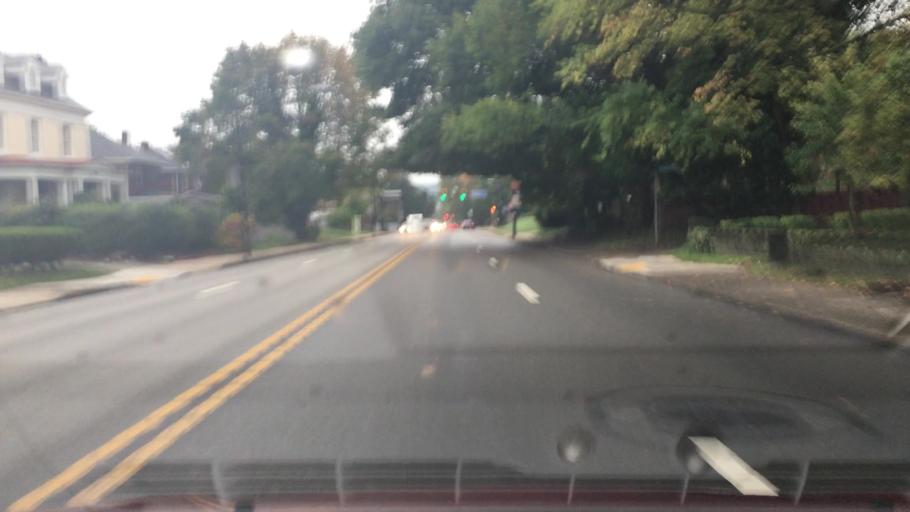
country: US
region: Pennsylvania
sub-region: Allegheny County
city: Wilkinsburg
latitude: 40.4496
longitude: -79.9028
